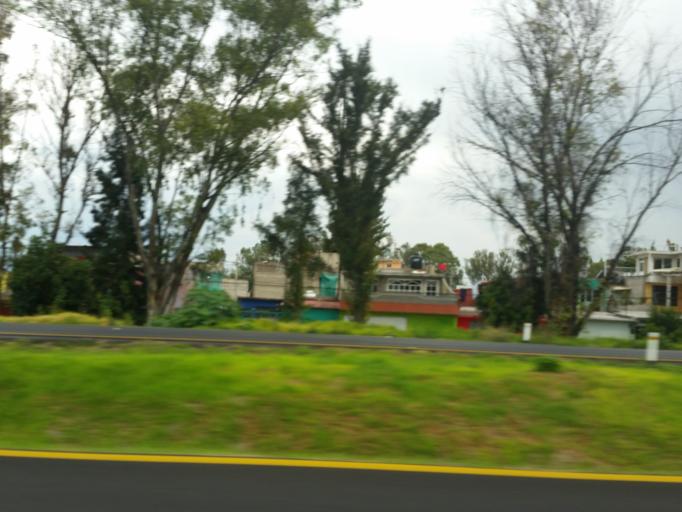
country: MX
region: Mexico
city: Santo Tomas Chiconautla
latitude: 19.6210
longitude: -99.0095
